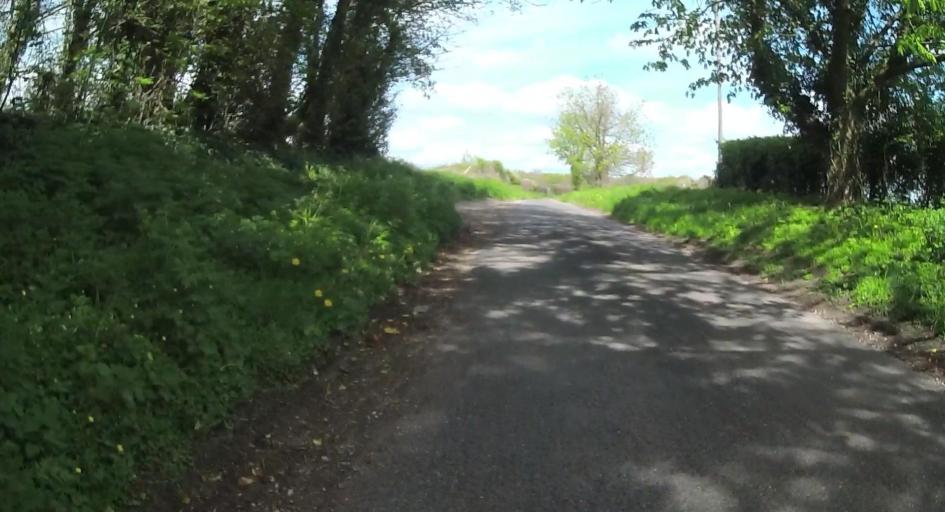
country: GB
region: England
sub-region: Hampshire
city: East Dean
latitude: 51.0658
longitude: -1.5321
